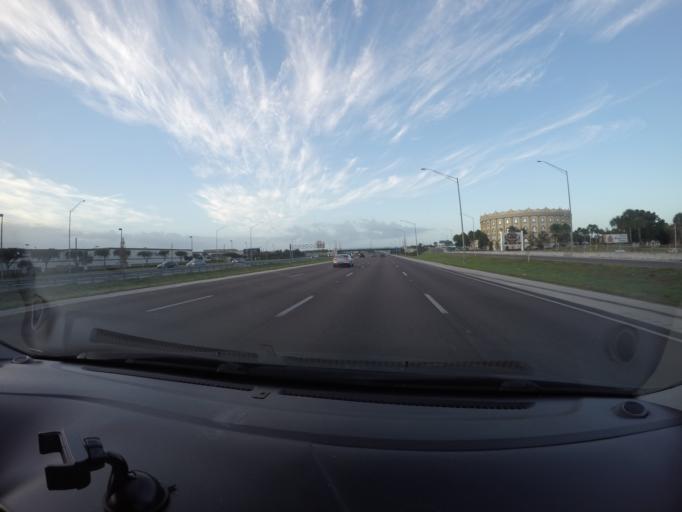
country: US
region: Florida
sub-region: Orange County
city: Oak Ridge
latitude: 28.4967
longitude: -81.4307
